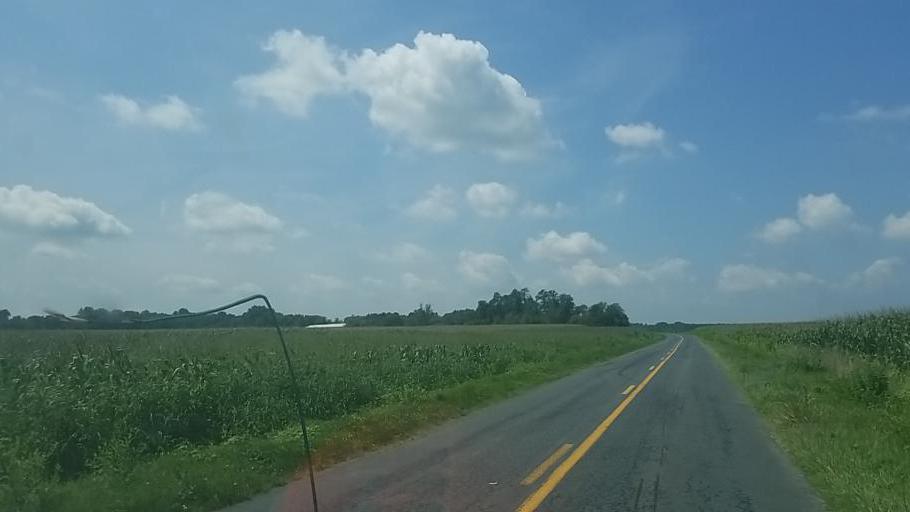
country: US
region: Maryland
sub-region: Talbot County
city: Easton
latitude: 38.7815
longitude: -76.0043
